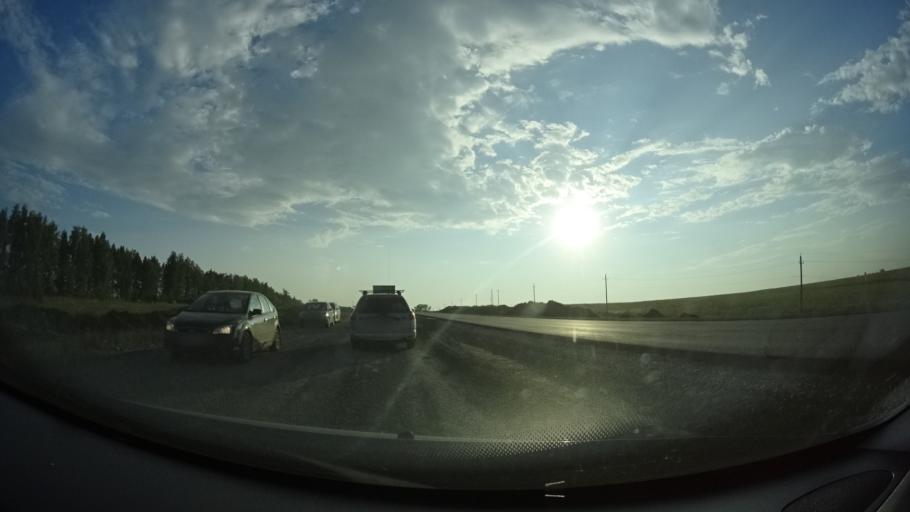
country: RU
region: Samara
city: Kamyshla
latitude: 54.0664
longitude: 52.1501
